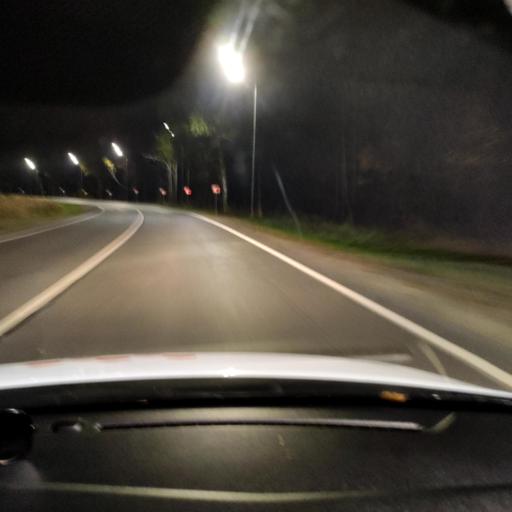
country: RU
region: Tatarstan
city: Stolbishchi
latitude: 55.6332
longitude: 49.0985
